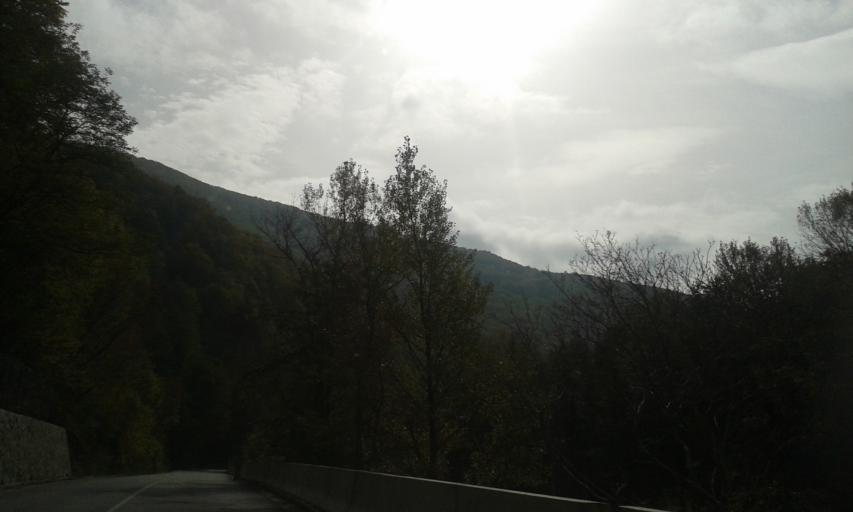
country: RO
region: Gorj
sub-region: Comuna Bumbesti-Jiu
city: Bumbesti-Jiu
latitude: 45.2350
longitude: 23.3897
